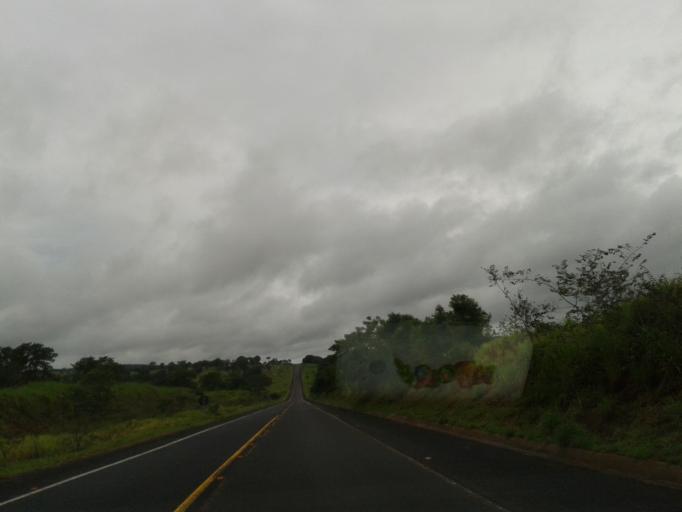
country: BR
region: Minas Gerais
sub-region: Santa Vitoria
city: Santa Vitoria
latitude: -19.2435
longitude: -50.0140
